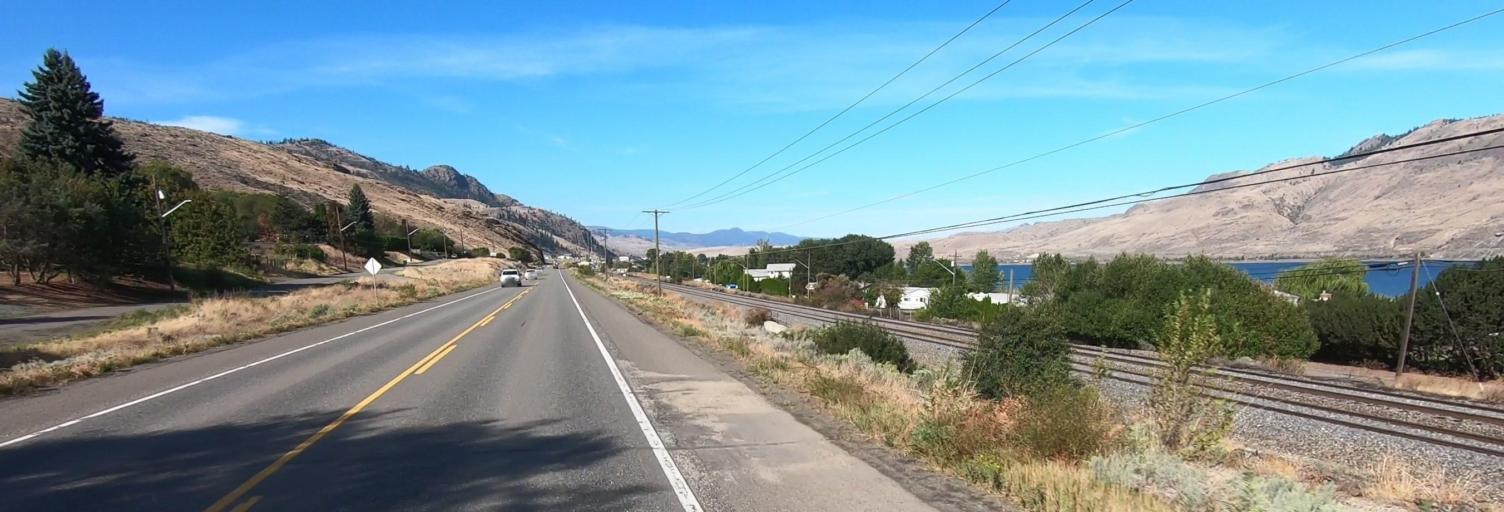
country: CA
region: British Columbia
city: Logan Lake
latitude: 50.7558
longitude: -120.8276
